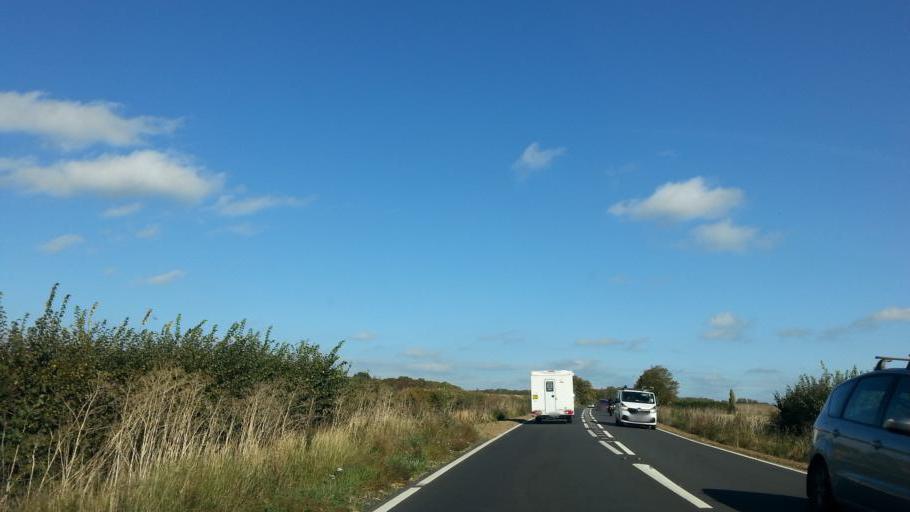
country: GB
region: England
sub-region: Northamptonshire
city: Oundle
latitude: 52.4294
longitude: -0.4862
